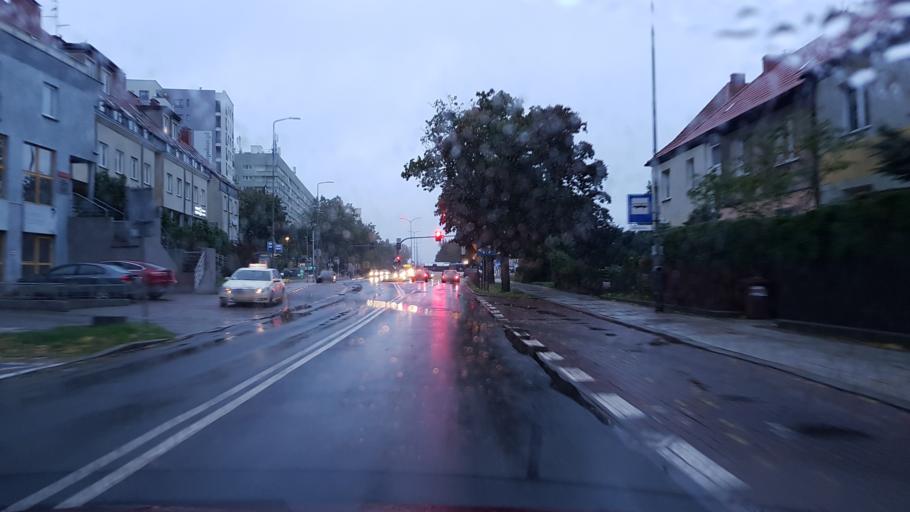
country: PL
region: West Pomeranian Voivodeship
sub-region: Szczecin
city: Szczecin
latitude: 53.4342
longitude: 14.5118
